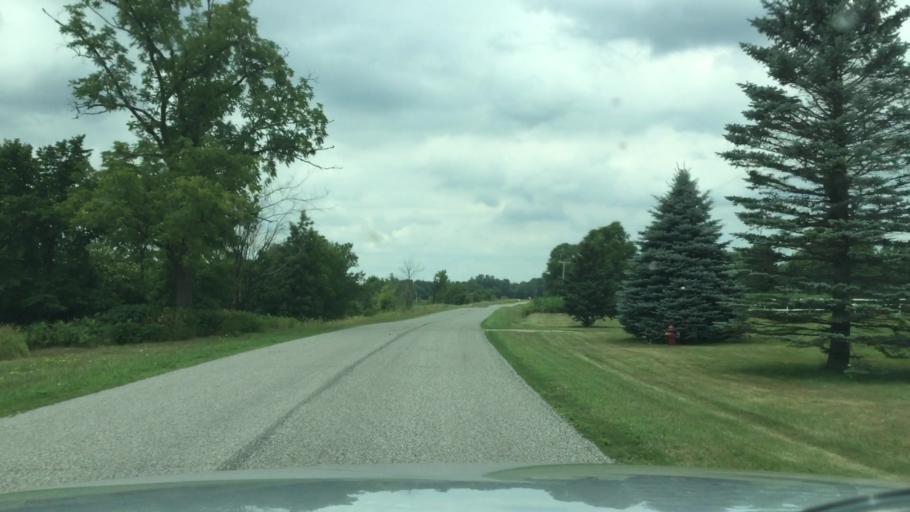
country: US
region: Michigan
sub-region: Saginaw County
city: Burt
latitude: 43.2701
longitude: -83.8841
